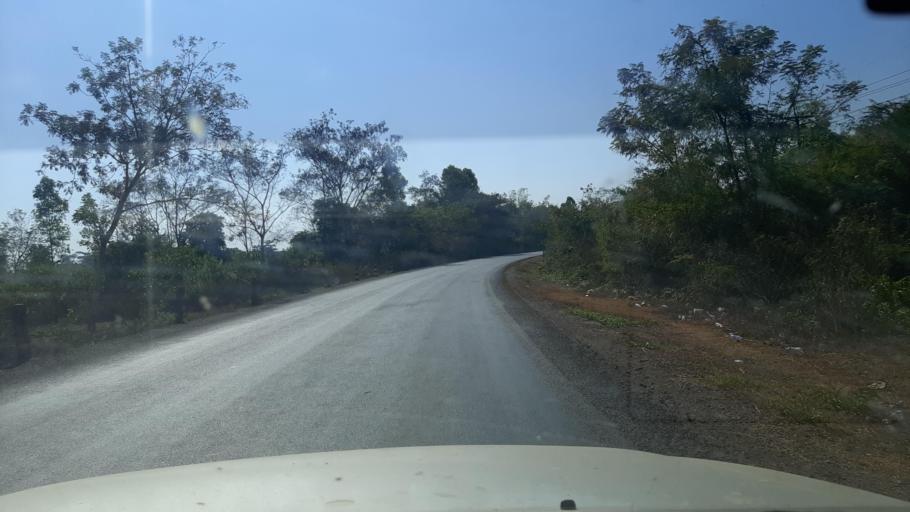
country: LA
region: Khammouan
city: Muang Hinboun
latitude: 17.5970
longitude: 104.6869
